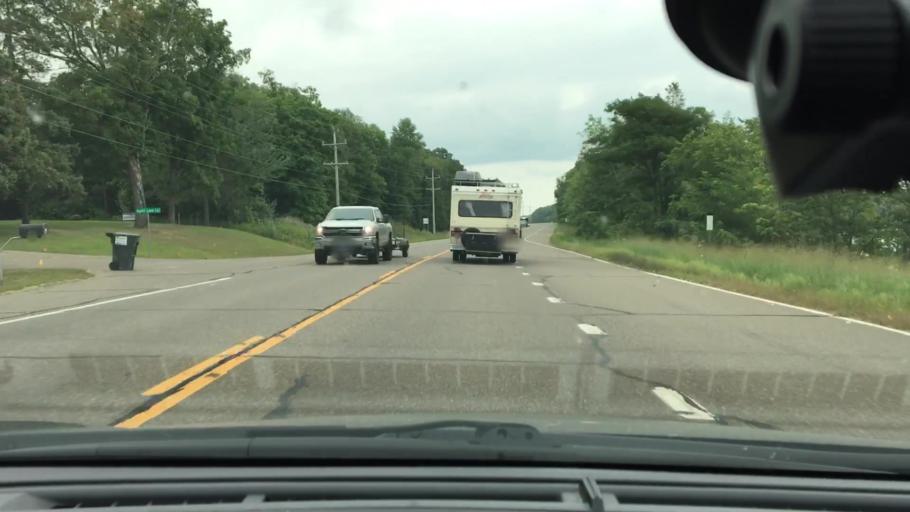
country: US
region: Minnesota
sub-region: Crow Wing County
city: Crosby
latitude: 46.4912
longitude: -93.9165
